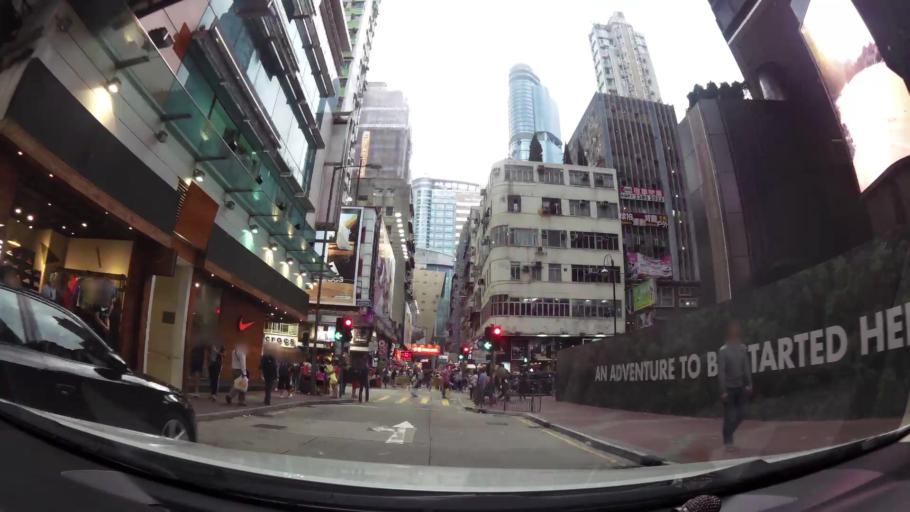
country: HK
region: Kowloon City
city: Kowloon
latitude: 22.3189
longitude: 114.1717
